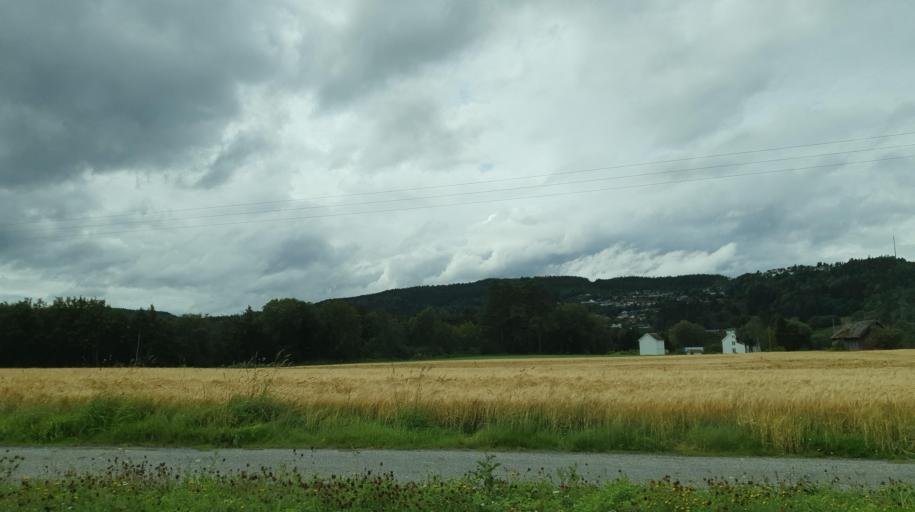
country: NO
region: Nord-Trondelag
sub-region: Stjordal
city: Stjordalshalsen
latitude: 63.4414
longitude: 10.9378
